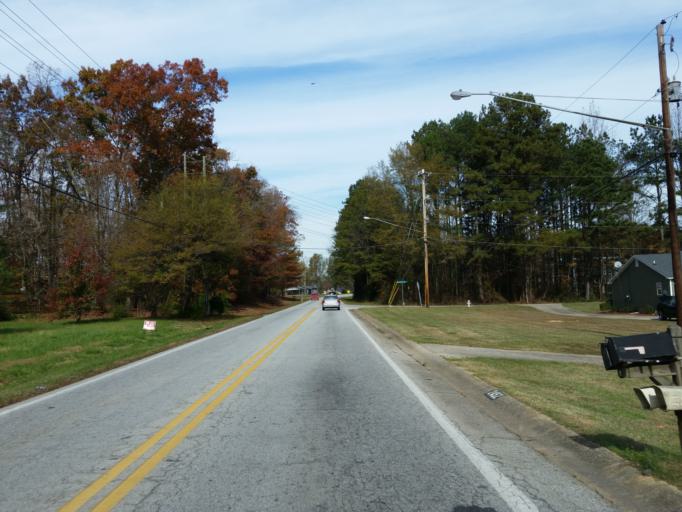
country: US
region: Georgia
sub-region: Douglas County
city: Lithia Springs
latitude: 33.7377
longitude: -84.6671
